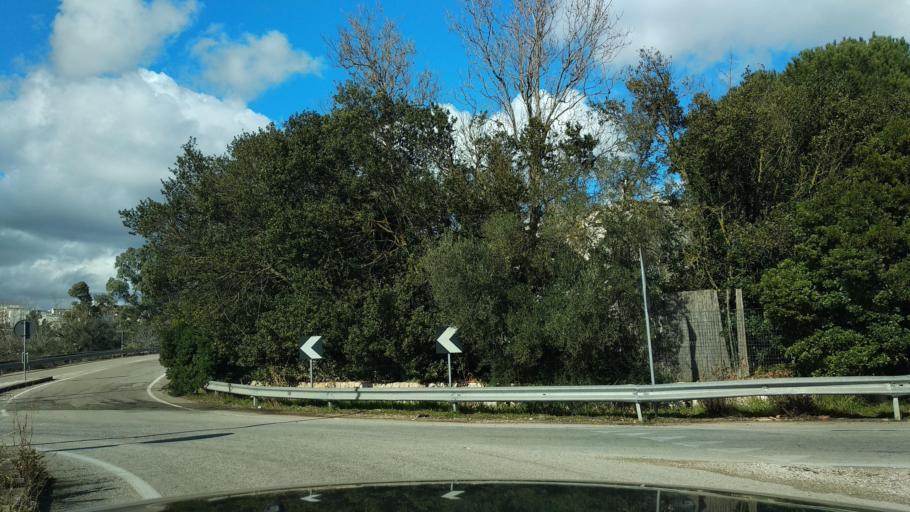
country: IT
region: Apulia
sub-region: Provincia di Brindisi
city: Cisternino
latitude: 40.7348
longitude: 17.4346
